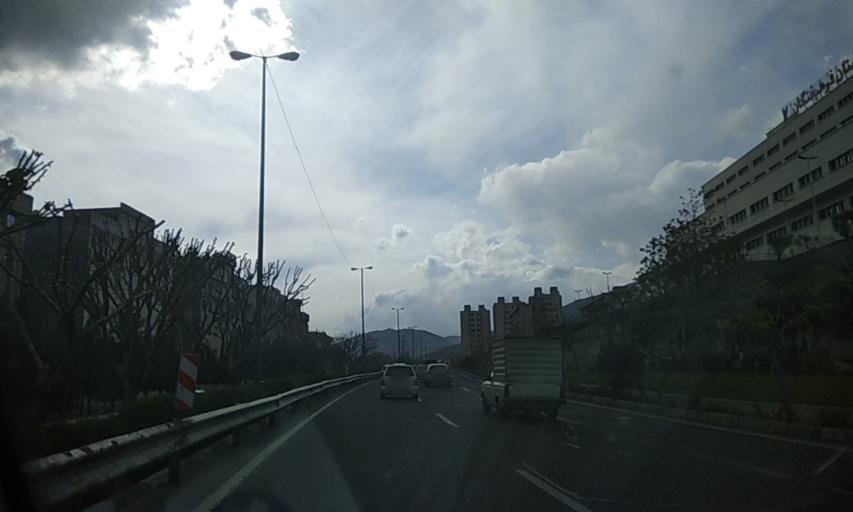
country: IR
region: Tehran
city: Tajrish
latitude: 35.7778
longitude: 51.3180
